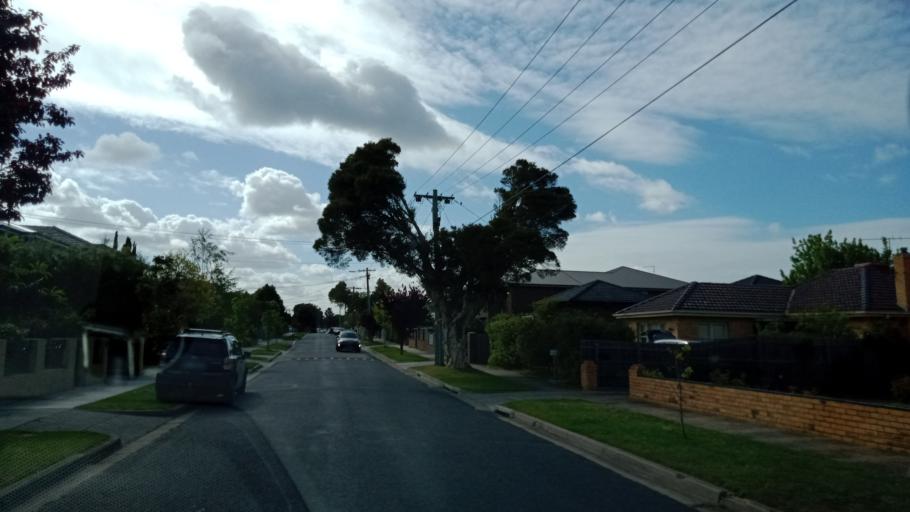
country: AU
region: Victoria
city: McKinnon
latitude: -37.9225
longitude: 145.0517
